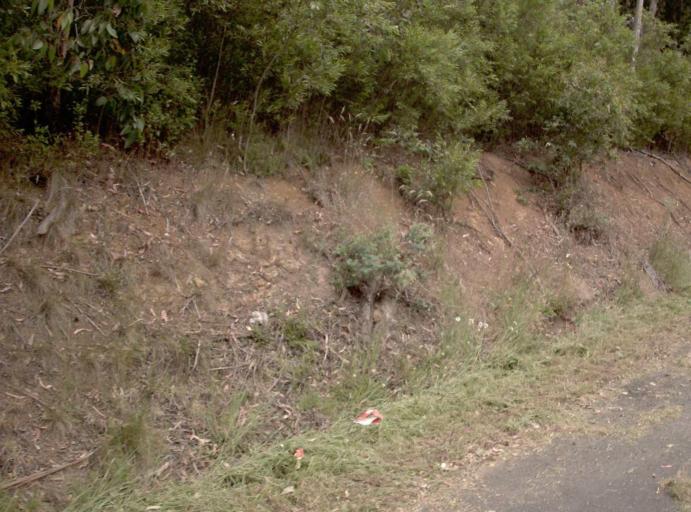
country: AU
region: Victoria
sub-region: Latrobe
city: Moe
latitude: -38.3110
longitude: 146.2687
